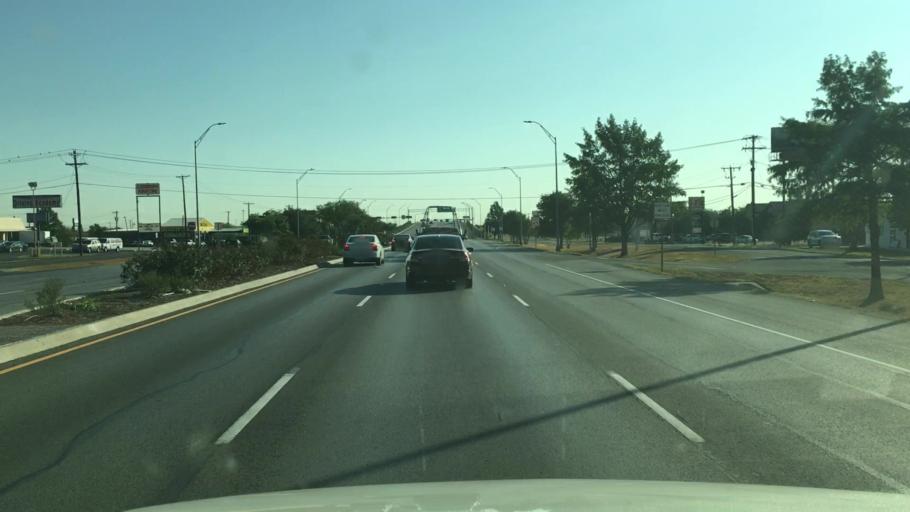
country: US
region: Texas
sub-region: Johnson County
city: Burleson
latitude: 32.5460
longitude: -97.3266
